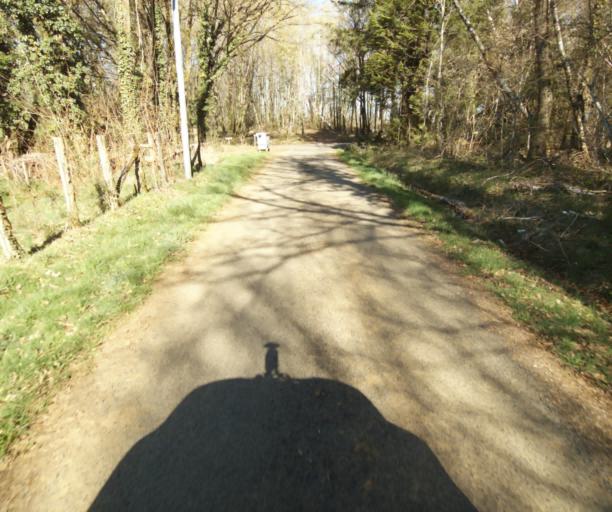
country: FR
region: Limousin
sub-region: Departement de la Correze
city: Chamboulive
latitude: 45.4105
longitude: 1.6867
